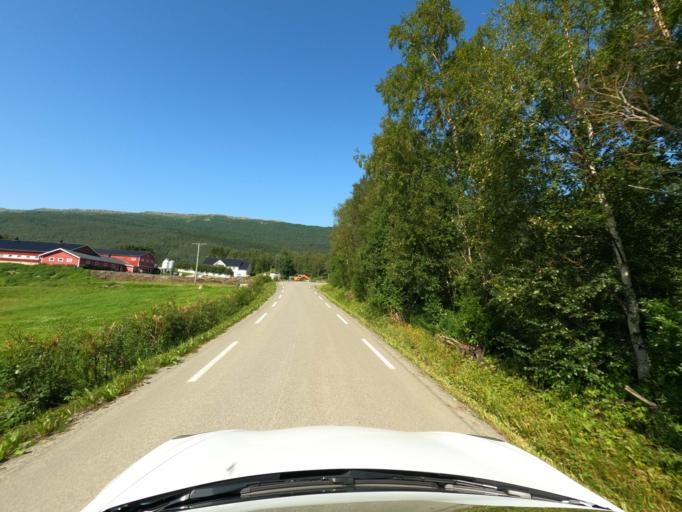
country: NO
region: Nordland
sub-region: Ballangen
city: Ballangen
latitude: 68.3458
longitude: 16.8061
